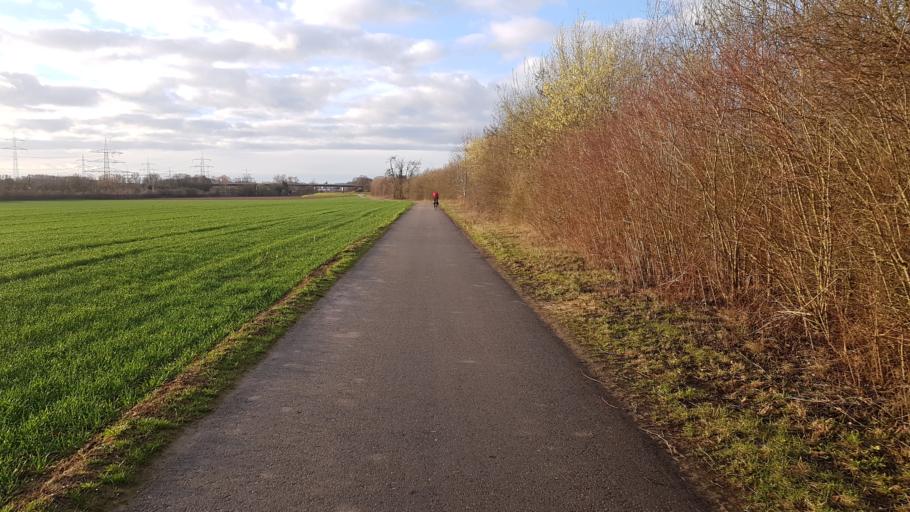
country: DE
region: Baden-Wuerttemberg
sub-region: Karlsruhe Region
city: Walldorf
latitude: 49.3160
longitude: 8.6650
